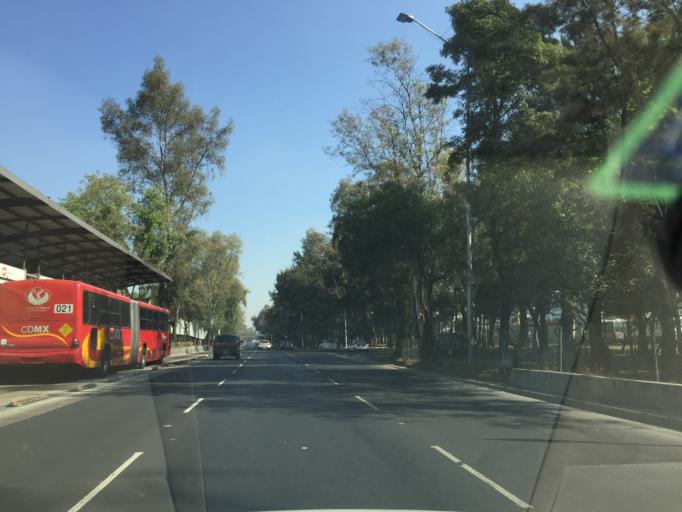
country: MX
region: Mexico
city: Colonia Lindavista
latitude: 19.4763
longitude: -99.1325
